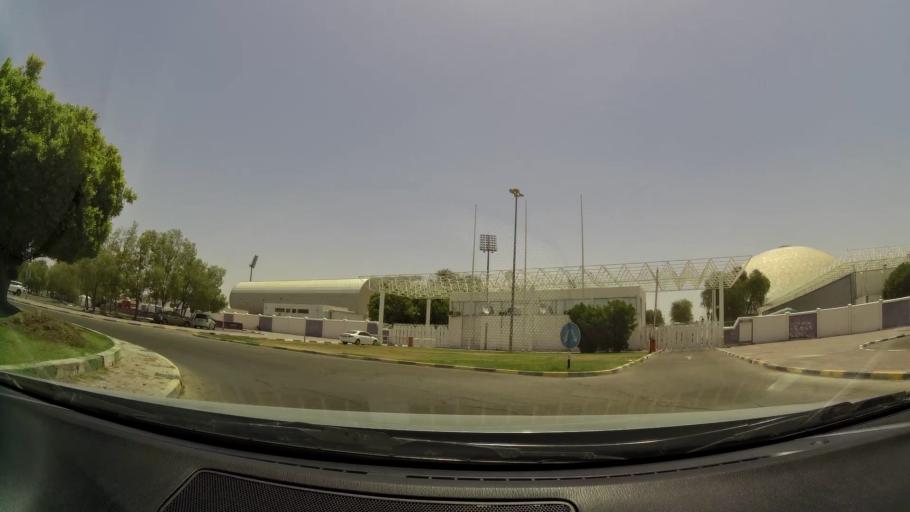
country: OM
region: Al Buraimi
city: Al Buraymi
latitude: 24.2676
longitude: 55.7543
